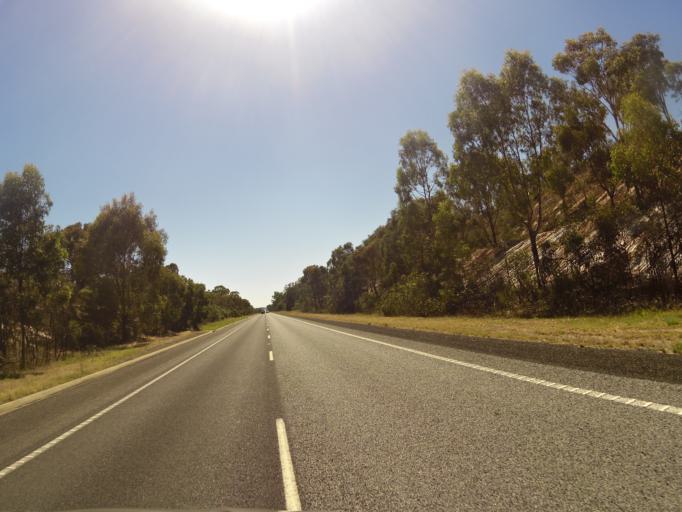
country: AU
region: Victoria
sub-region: Greater Shepparton
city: Shepparton
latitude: -36.8539
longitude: 145.3265
